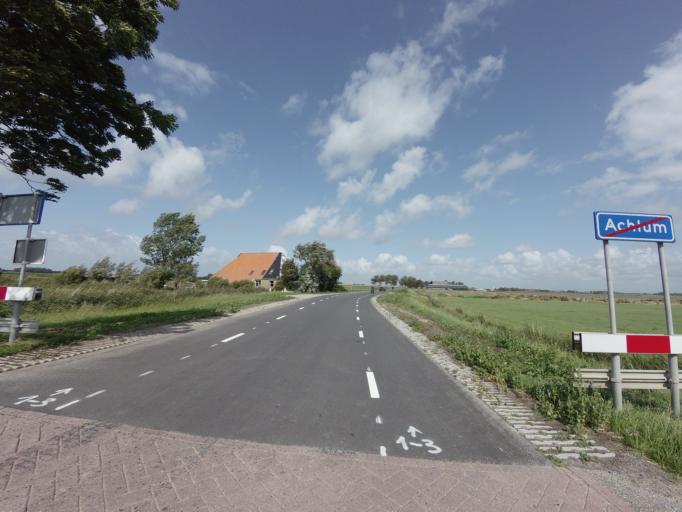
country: NL
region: Friesland
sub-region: Gemeente Harlingen
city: Harlingen
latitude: 53.1507
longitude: 5.4770
